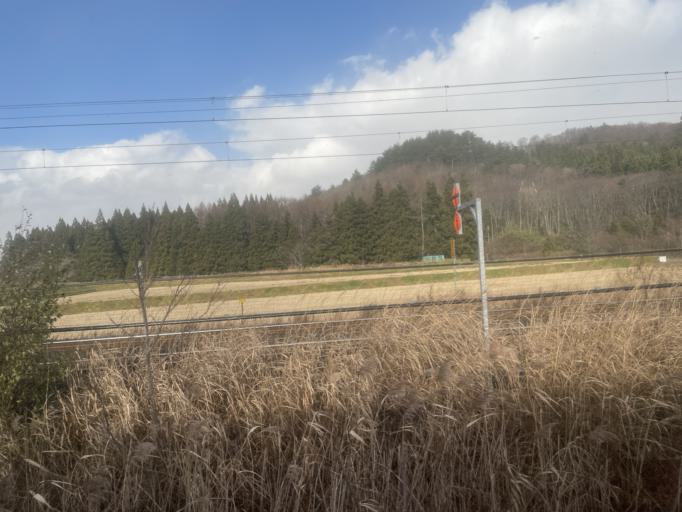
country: JP
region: Aomori
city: Goshogawara
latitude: 41.0657
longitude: 140.5688
